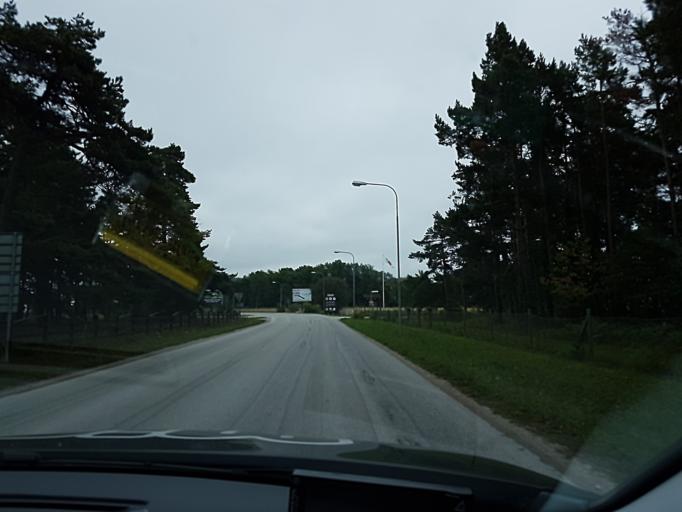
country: SE
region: Gotland
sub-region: Gotland
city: Visby
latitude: 57.6612
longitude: 18.3328
